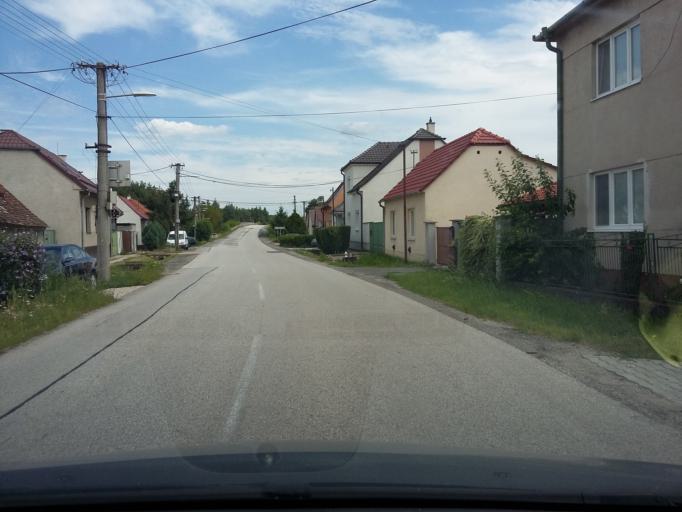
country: SK
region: Bratislavsky
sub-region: Okres Malacky
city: Malacky
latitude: 48.4414
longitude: 17.0396
